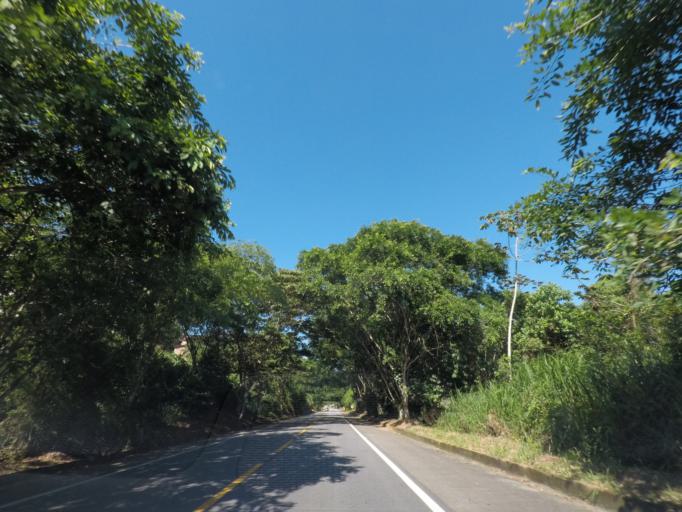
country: BR
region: Rio de Janeiro
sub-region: Parati
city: Paraty
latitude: -23.3092
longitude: -44.7113
